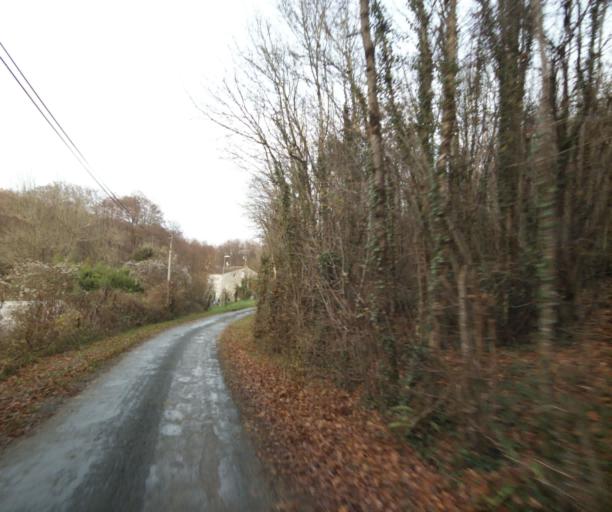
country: FR
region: Poitou-Charentes
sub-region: Departement de la Charente-Maritime
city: Bussac-sur-Charente
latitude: 45.8108
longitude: -0.6031
